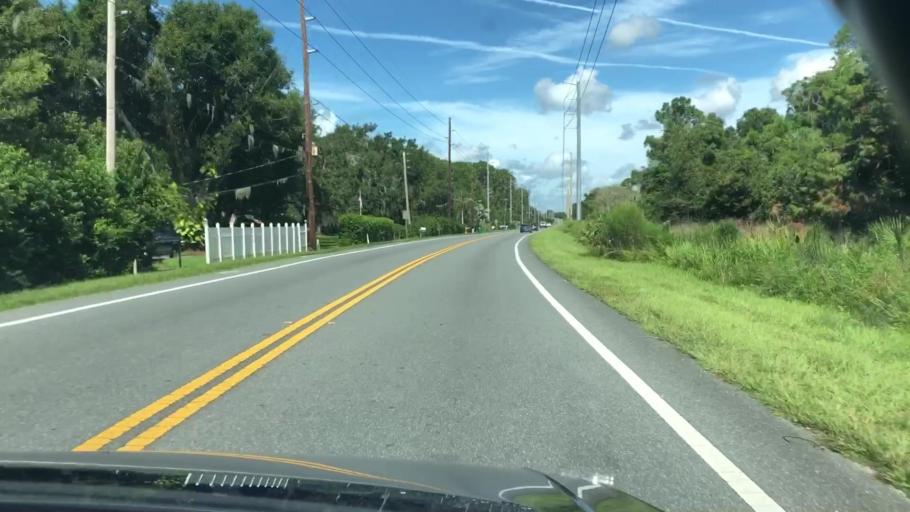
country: US
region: Florida
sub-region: Lake County
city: Eustis
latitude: 28.8747
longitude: -81.7058
